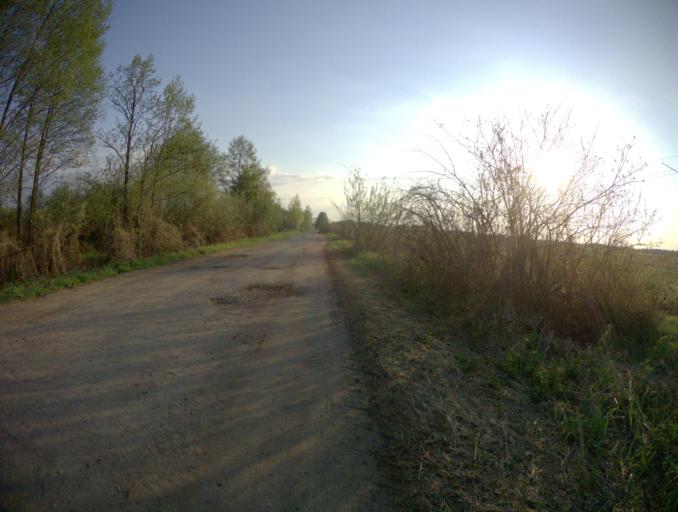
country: RU
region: Vladimir
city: Vyazniki
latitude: 56.3193
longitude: 42.1076
